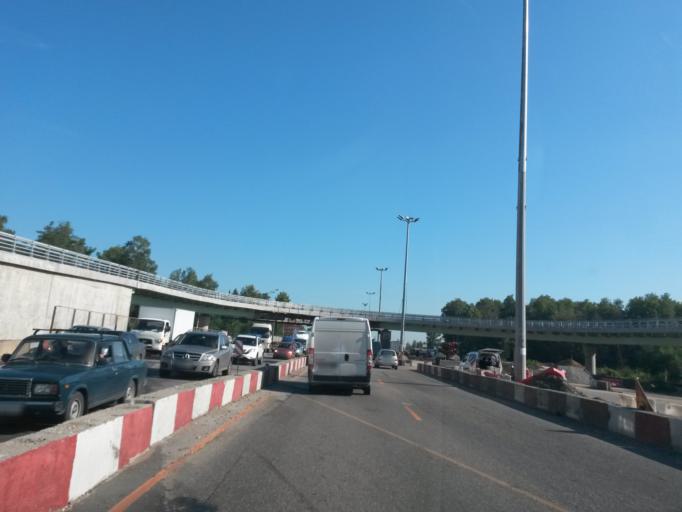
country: RU
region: Moskovskaya
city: Bolshevo
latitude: 55.9403
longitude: 37.8124
